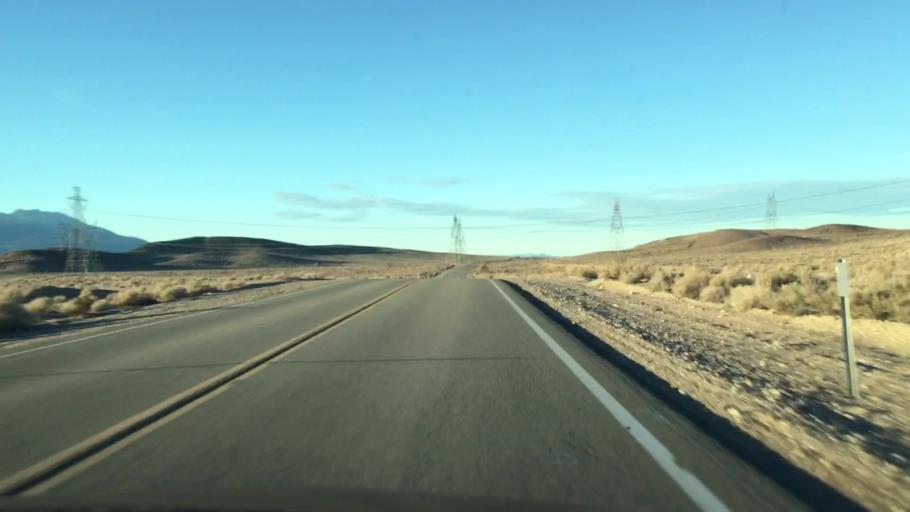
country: US
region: California
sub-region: San Bernardino County
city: Fort Irwin
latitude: 35.3820
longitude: -116.1240
